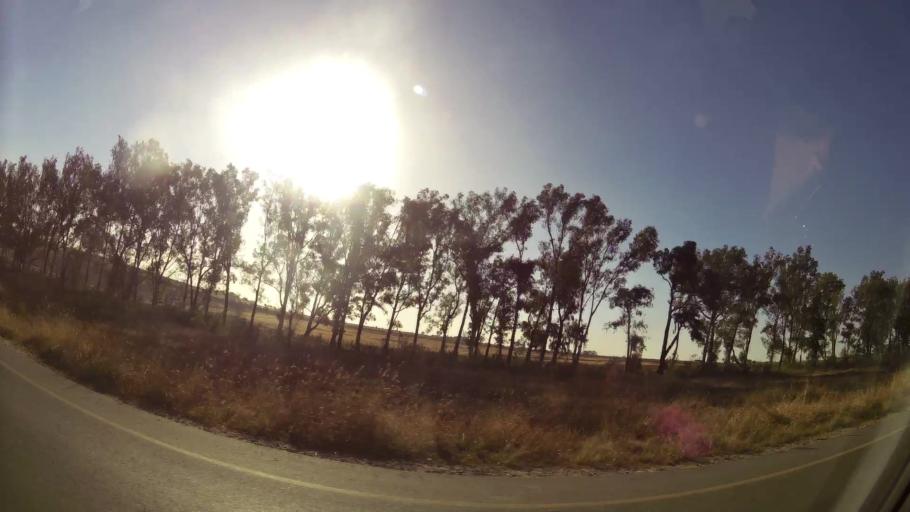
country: ZA
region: Gauteng
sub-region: City of Johannesburg Metropolitan Municipality
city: Diepsloot
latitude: -25.9412
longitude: 27.9814
